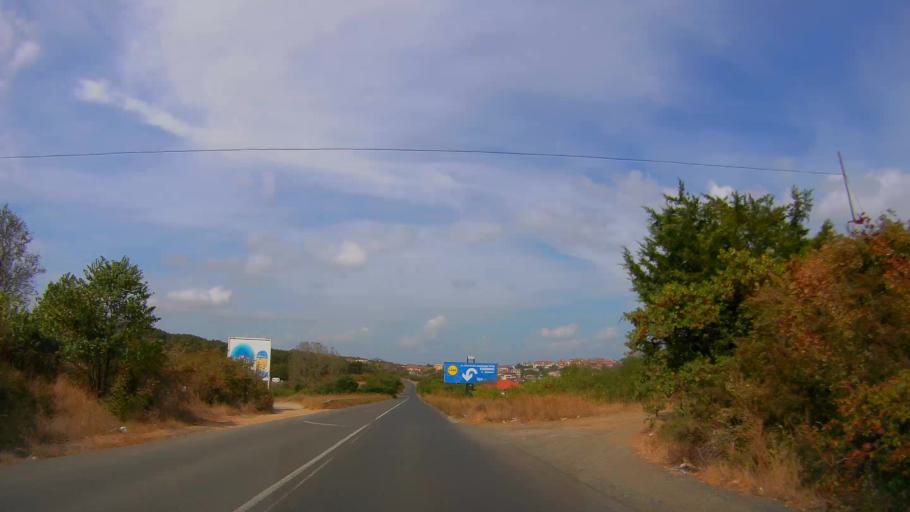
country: BG
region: Burgas
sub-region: Obshtina Sozopol
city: Sozopol
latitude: 42.4078
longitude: 27.7007
